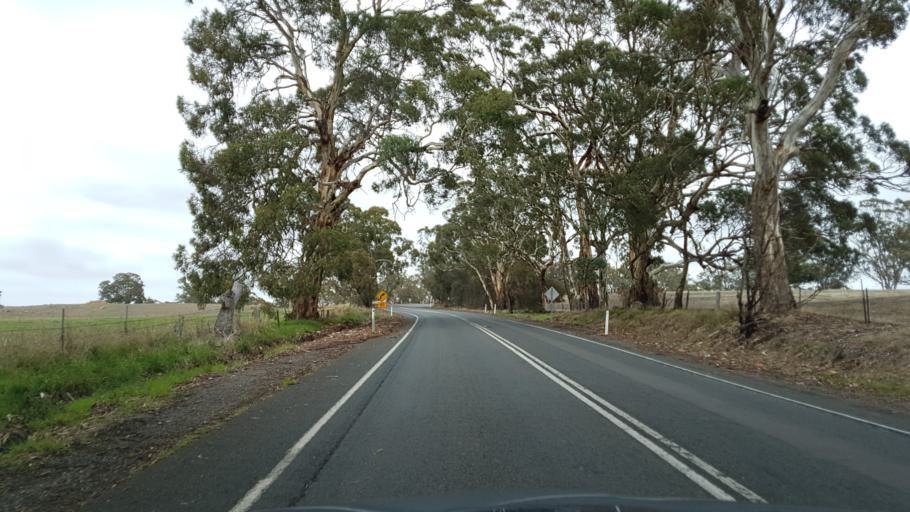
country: AU
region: South Australia
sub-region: Mount Barker
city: Nairne
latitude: -35.0406
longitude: 138.9391
